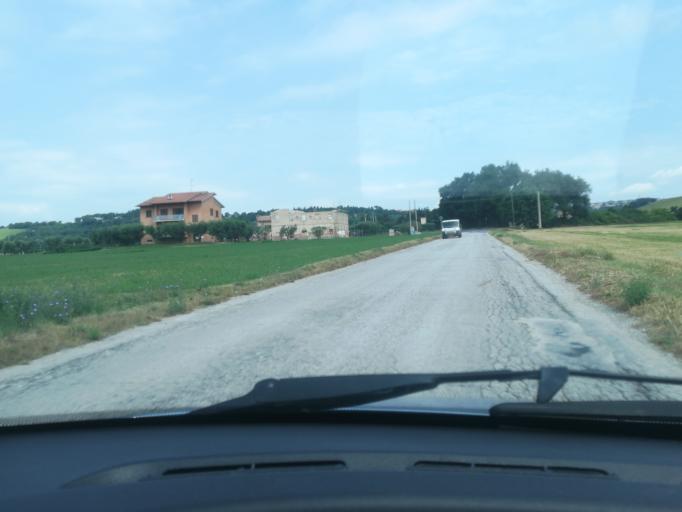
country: IT
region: The Marches
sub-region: Provincia di Macerata
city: Sforzacosta
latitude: 43.2677
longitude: 13.4385
